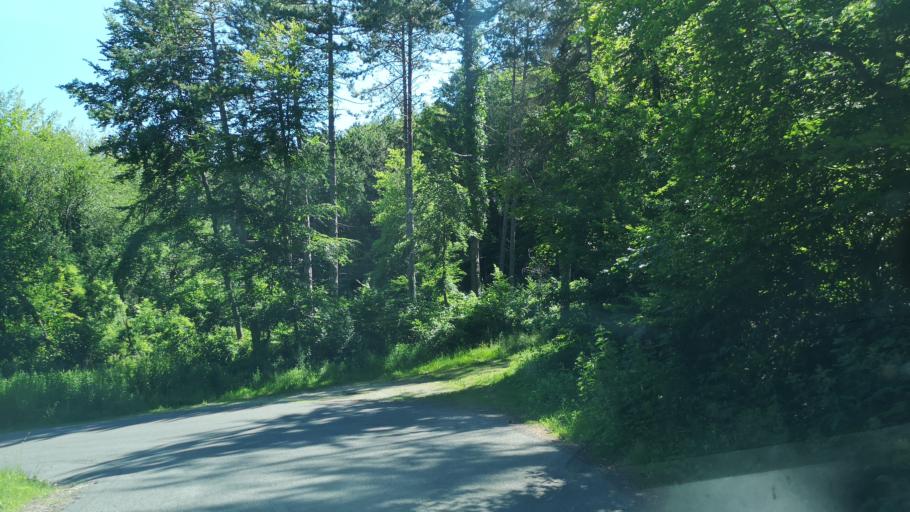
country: FR
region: Lorraine
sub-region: Departement de la Meuse
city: Vigneulles-les-Hattonchatel
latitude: 49.0307
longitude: 5.6527
